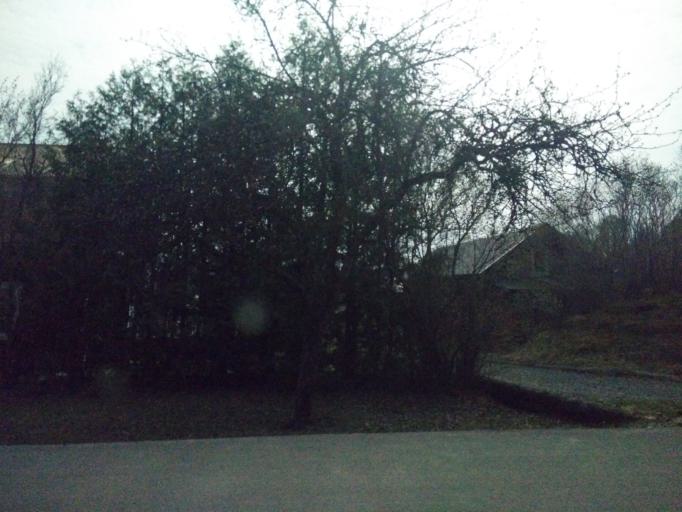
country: SE
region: Vaermland
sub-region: Munkfors Kommun
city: Munkfors
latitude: 59.8352
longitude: 13.5125
